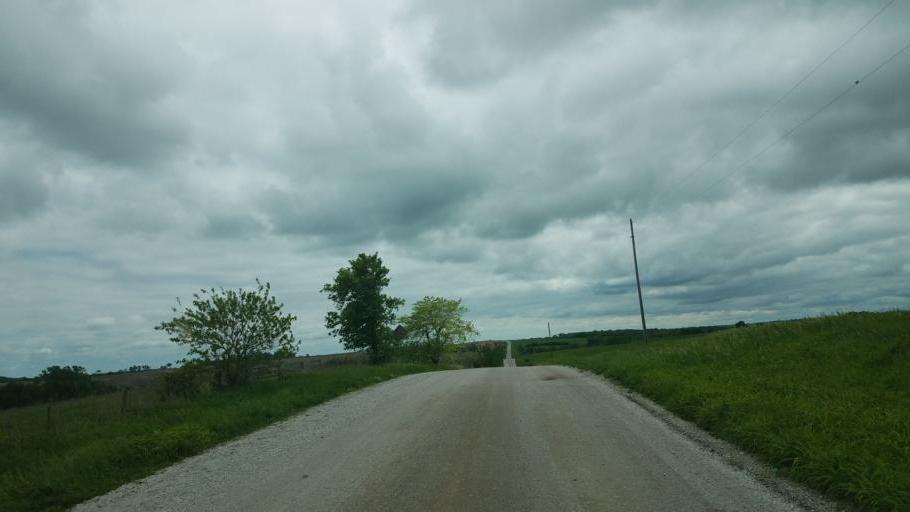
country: US
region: Iowa
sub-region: Decatur County
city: Lamoni
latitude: 40.5931
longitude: -93.8537
